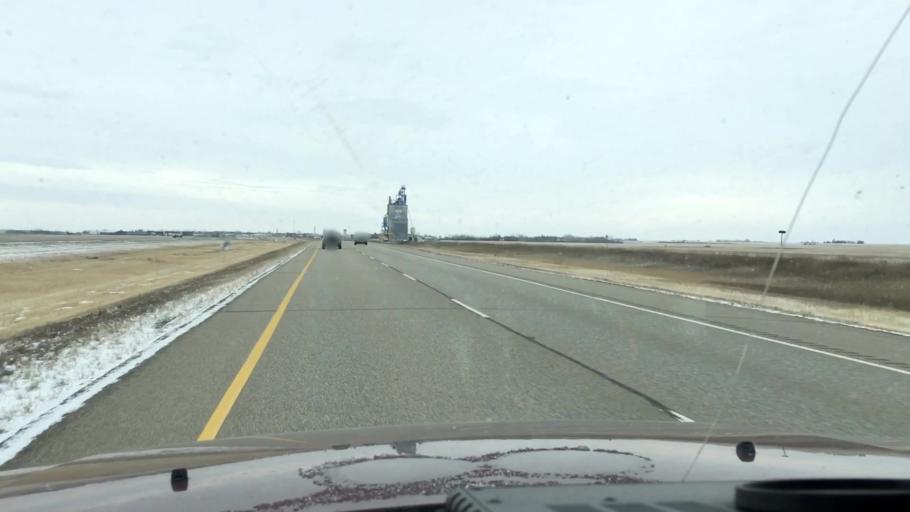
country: CA
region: Saskatchewan
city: Watrous
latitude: 51.2869
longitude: -106.0245
